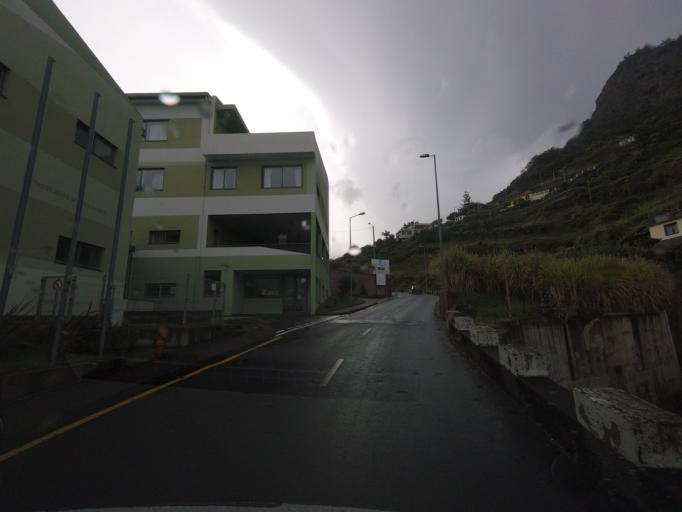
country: PT
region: Madeira
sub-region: Santana
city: Santana
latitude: 32.7718
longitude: -16.8312
